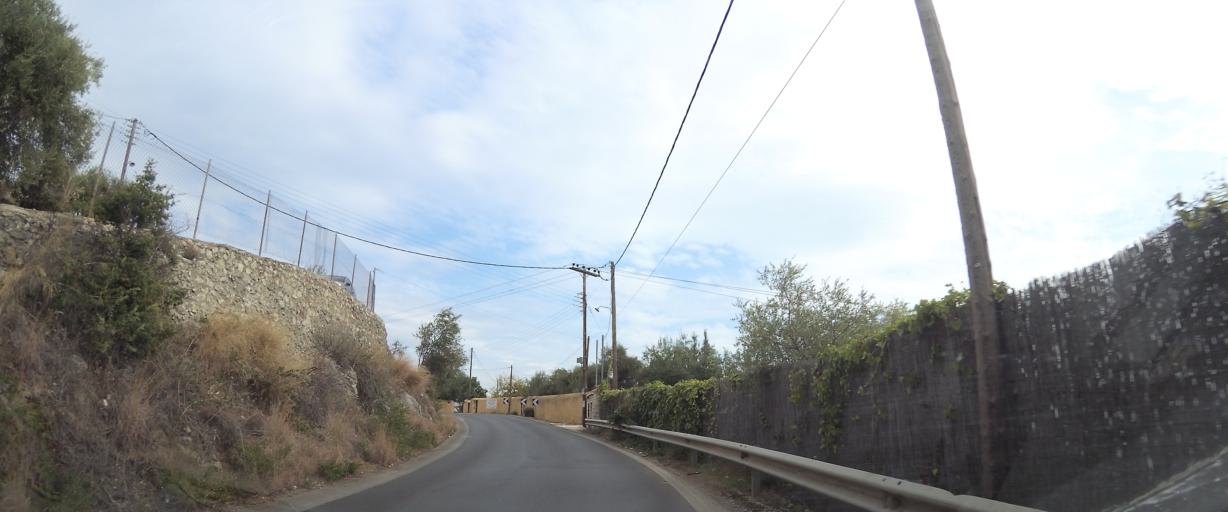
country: GR
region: Ionian Islands
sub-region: Nomos Kerkyras
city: Kontokali
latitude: 39.7096
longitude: 19.8551
